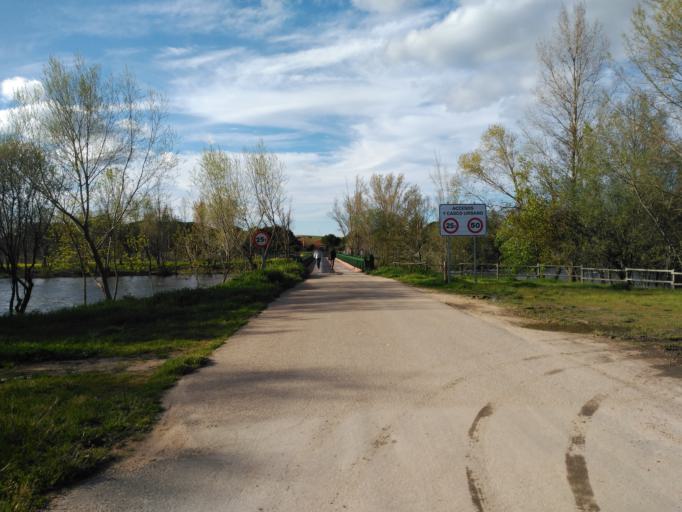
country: ES
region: Castille and Leon
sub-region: Provincia de Salamanca
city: Almenara de Tormes
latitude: 41.0569
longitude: -5.8260
